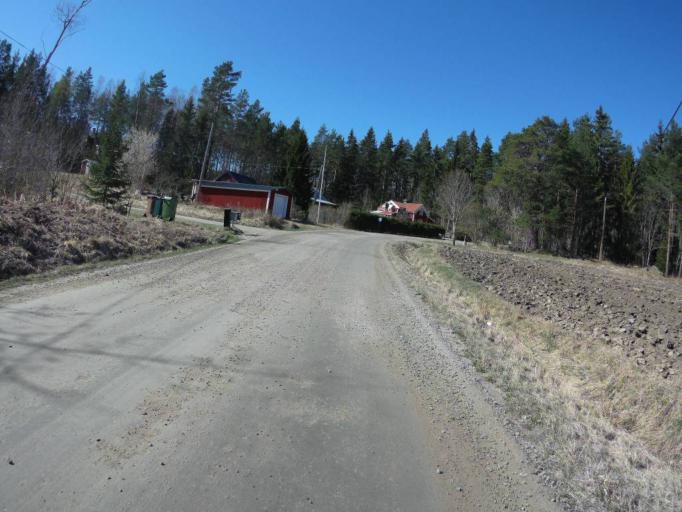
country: SE
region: Gaevleborg
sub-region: Gavle Kommun
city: Gavle
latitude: 60.7302
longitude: 17.2006
